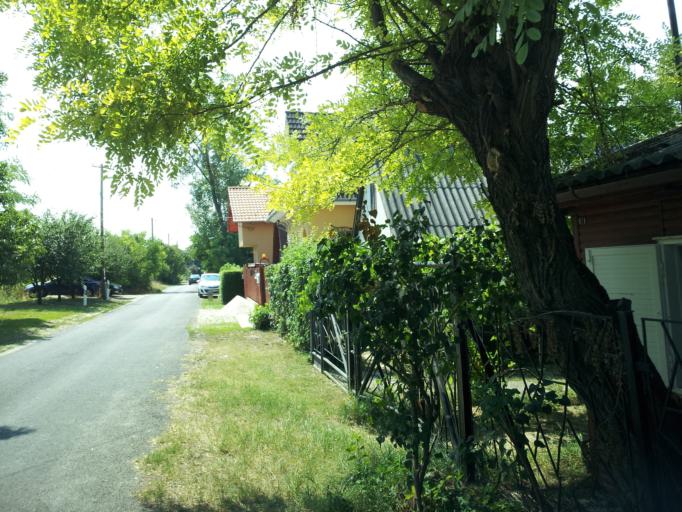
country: HU
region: Pest
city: Szigethalom
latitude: 47.2991
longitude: 19.0265
